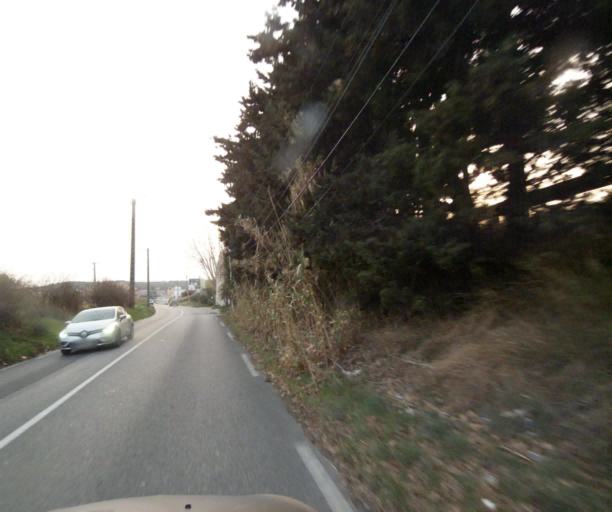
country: FR
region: Provence-Alpes-Cote d'Azur
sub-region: Departement des Bouches-du-Rhone
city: Cabries
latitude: 43.4242
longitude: 5.3689
